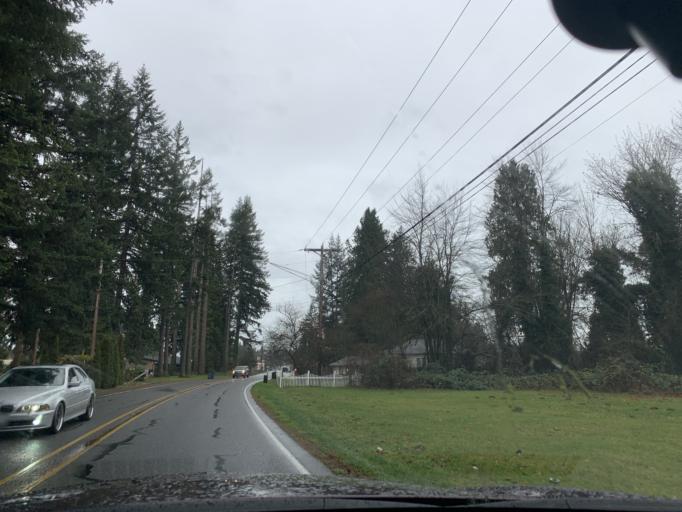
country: US
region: Washington
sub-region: Snohomish County
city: Marysville
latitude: 48.0885
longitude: -122.1673
